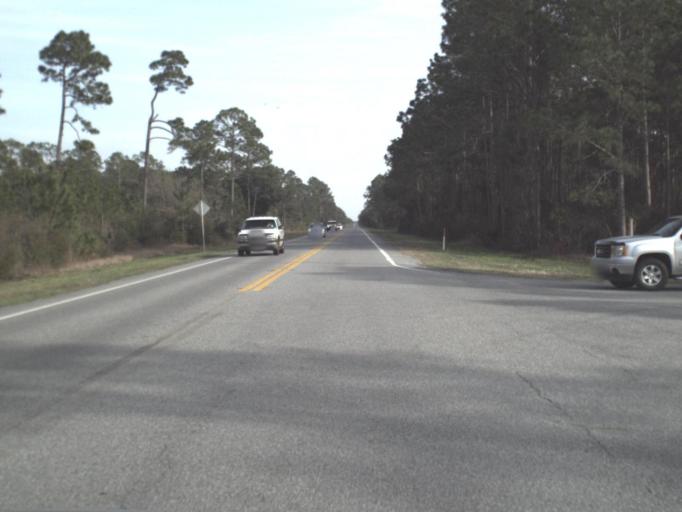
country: US
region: Florida
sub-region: Bay County
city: Mexico Beach
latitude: 29.9752
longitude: -85.4648
